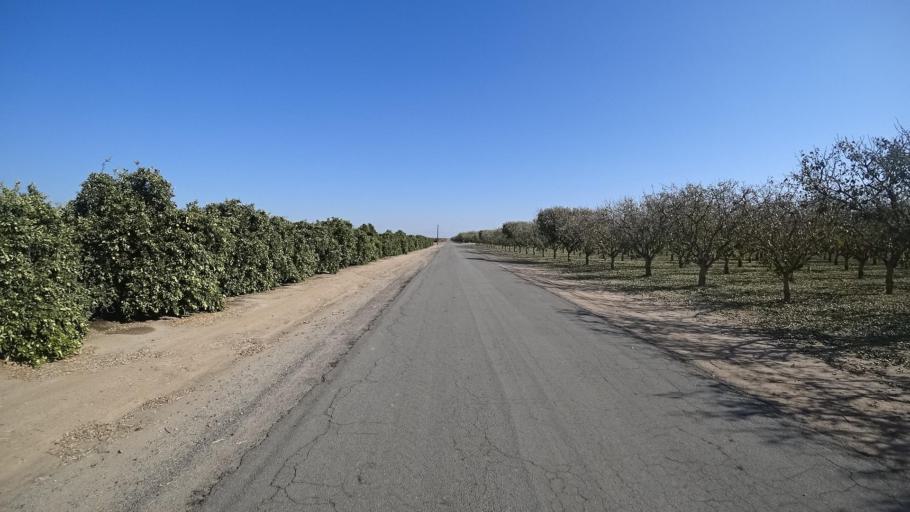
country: US
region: California
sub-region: Kern County
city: McFarland
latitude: 35.6456
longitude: -119.1710
